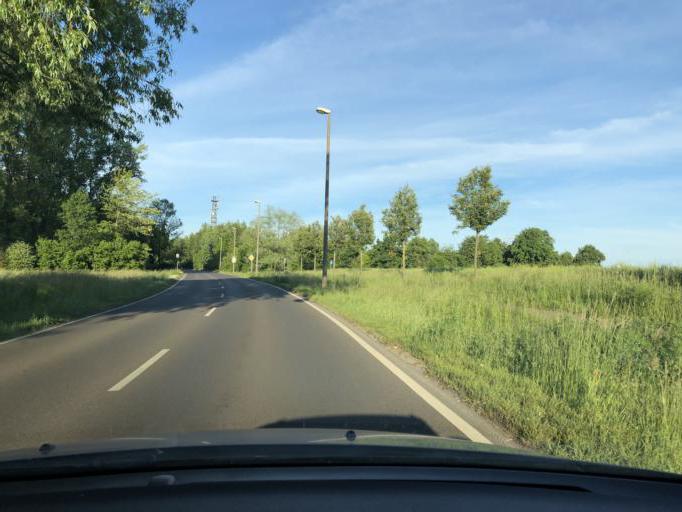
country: DE
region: Saxony
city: Markkleeberg
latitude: 51.2847
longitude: 12.4138
